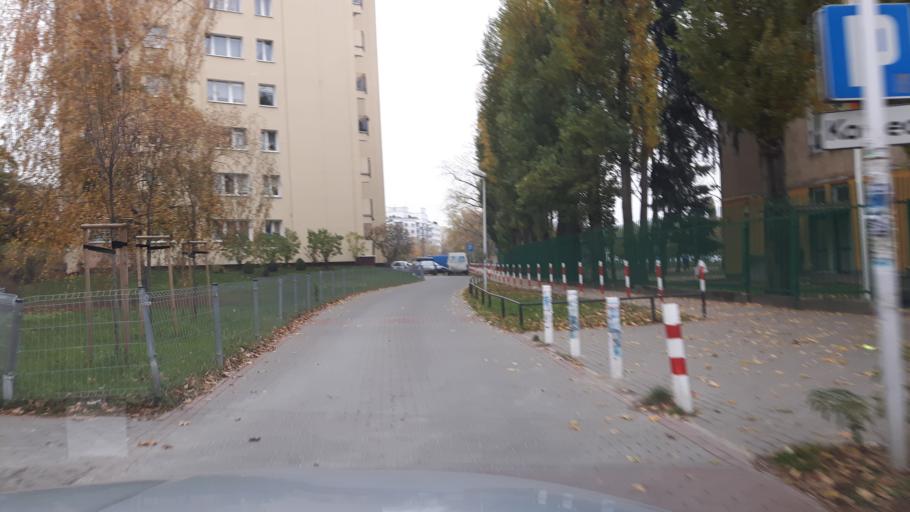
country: PL
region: Masovian Voivodeship
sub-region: Warszawa
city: Targowek
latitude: 52.2748
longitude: 21.0449
